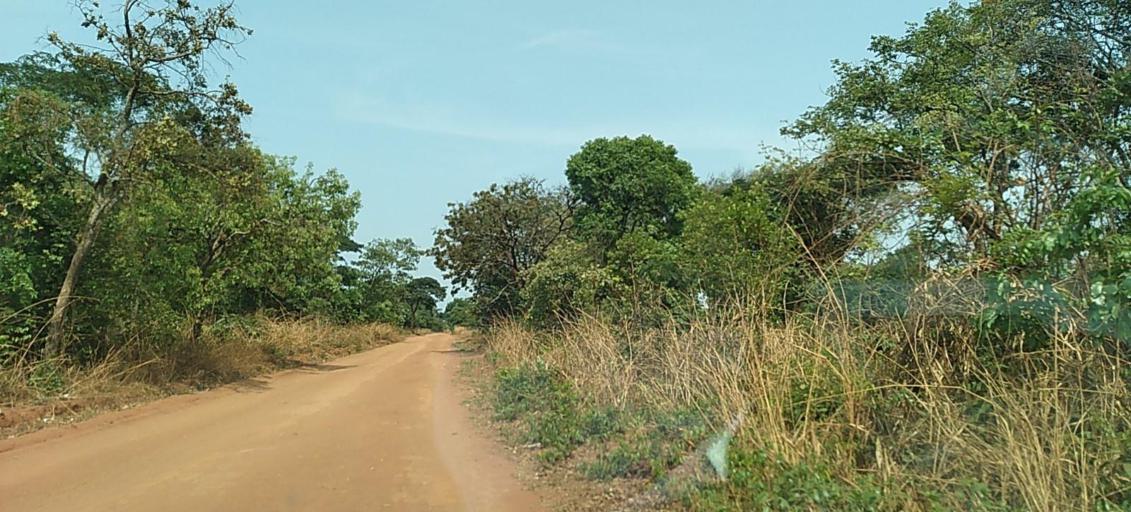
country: ZM
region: Copperbelt
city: Chililabombwe
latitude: -12.3405
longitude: 27.6918
